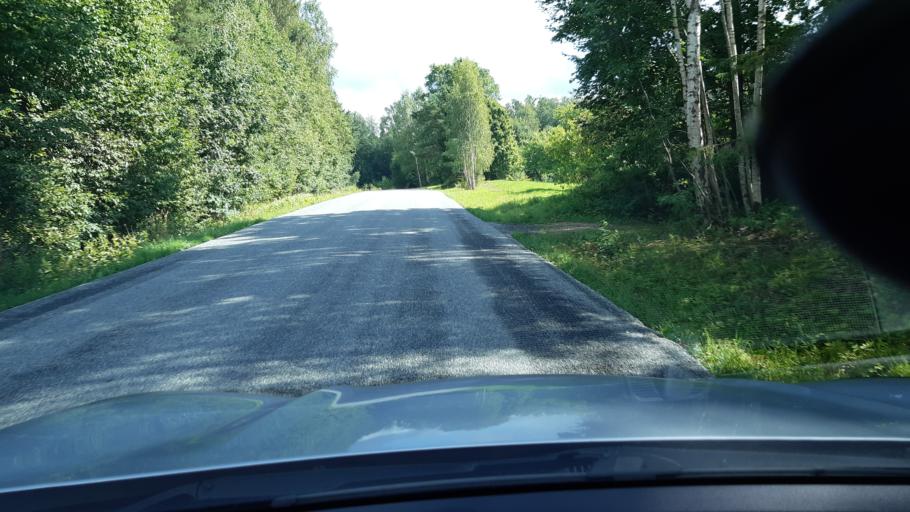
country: EE
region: Raplamaa
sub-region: Kehtna vald
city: Kehtna
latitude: 58.9035
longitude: 25.0714
